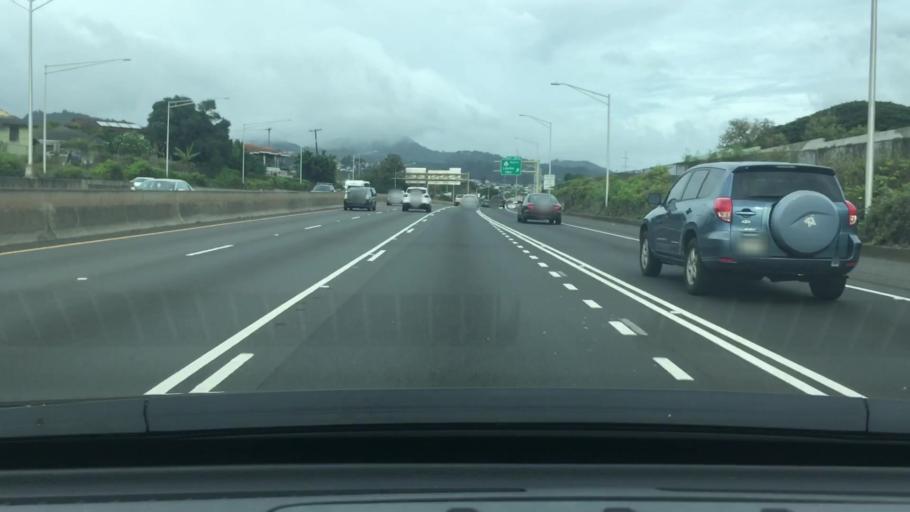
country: US
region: Hawaii
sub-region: Honolulu County
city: Honolulu
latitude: 21.3361
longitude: -157.8801
